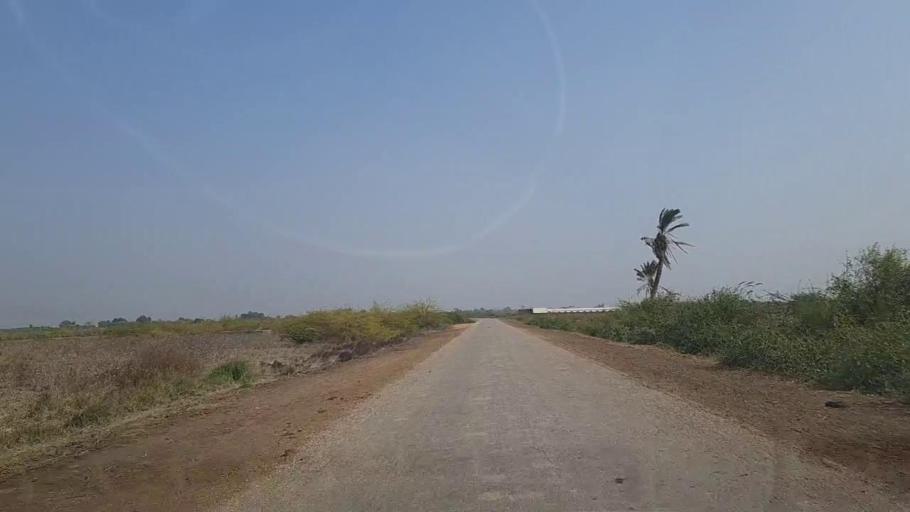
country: PK
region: Sindh
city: Keti Bandar
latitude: 24.2493
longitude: 67.7148
